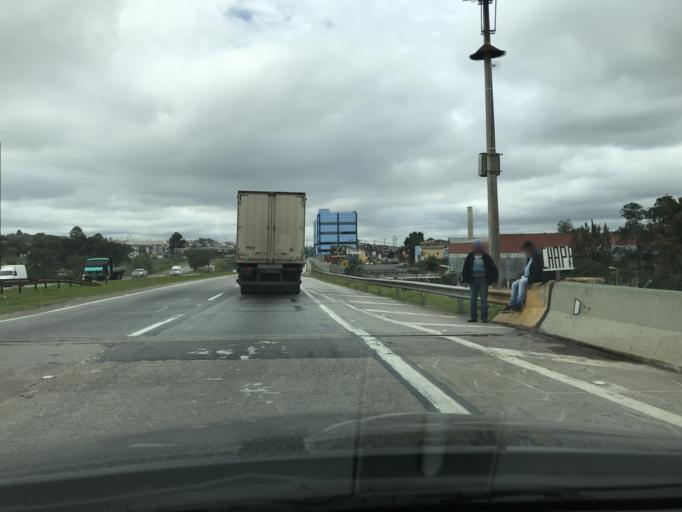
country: BR
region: Sao Paulo
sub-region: Itaquaquecetuba
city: Itaquaquecetuba
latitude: -23.4628
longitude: -46.3383
